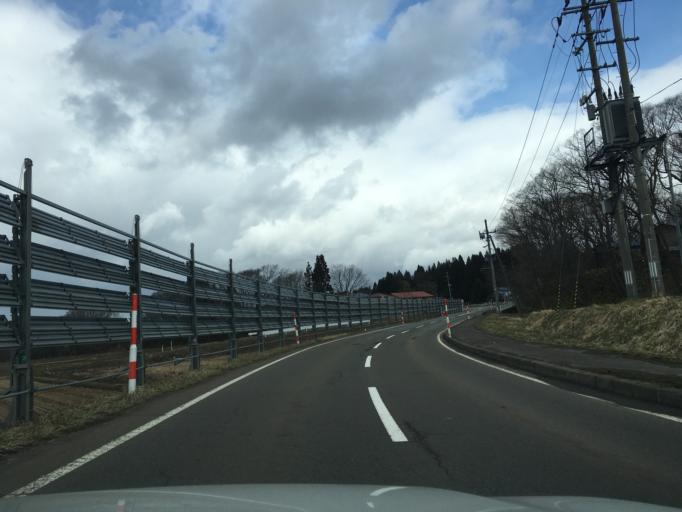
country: JP
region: Akita
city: Takanosu
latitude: 40.1530
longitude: 140.3354
